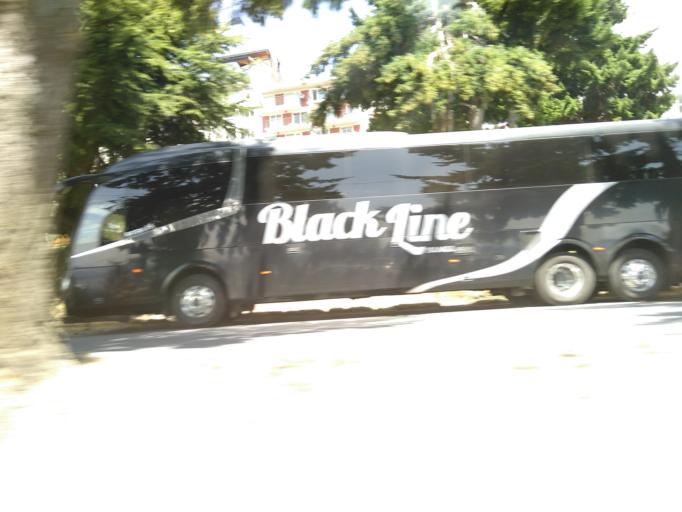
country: AR
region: Rio Negro
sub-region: Departamento de Bariloche
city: San Carlos de Bariloche
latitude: -41.1326
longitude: -71.3045
